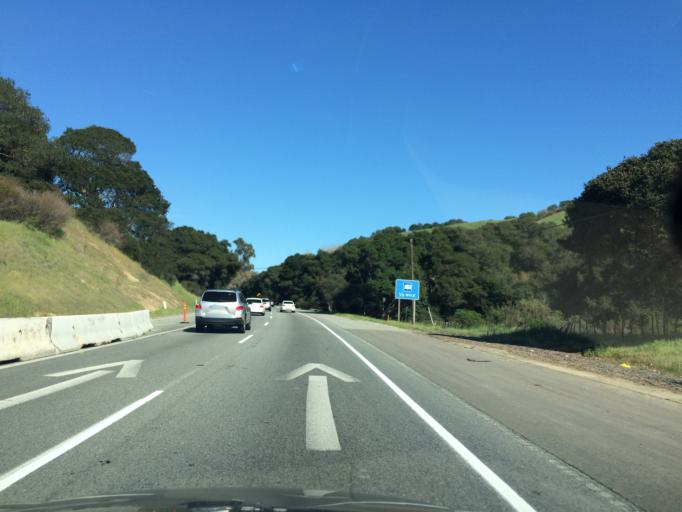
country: US
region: California
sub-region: San Benito County
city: Aromas
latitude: 36.8600
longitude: -121.6220
